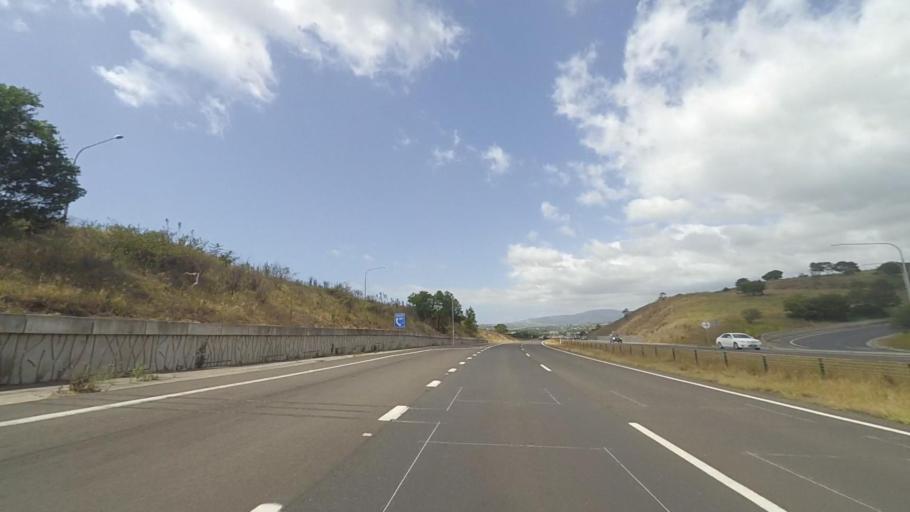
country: AU
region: New South Wales
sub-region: Shellharbour
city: Croom
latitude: -34.5892
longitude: 150.8446
